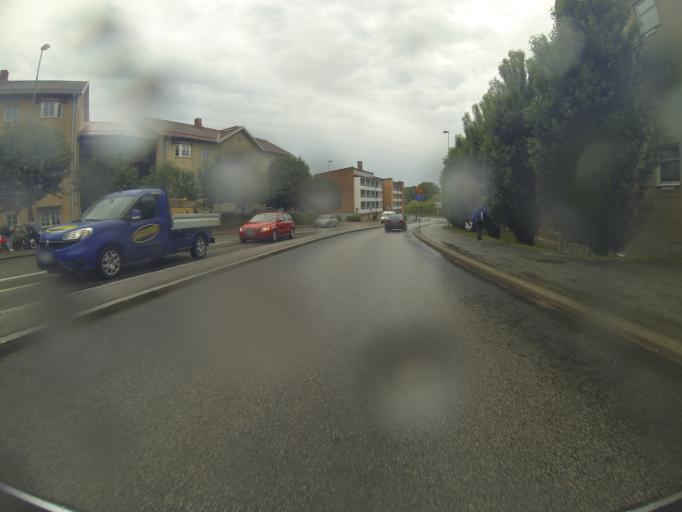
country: SE
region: Blekinge
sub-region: Ronneby Kommun
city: Ronneby
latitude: 56.2101
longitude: 15.2822
